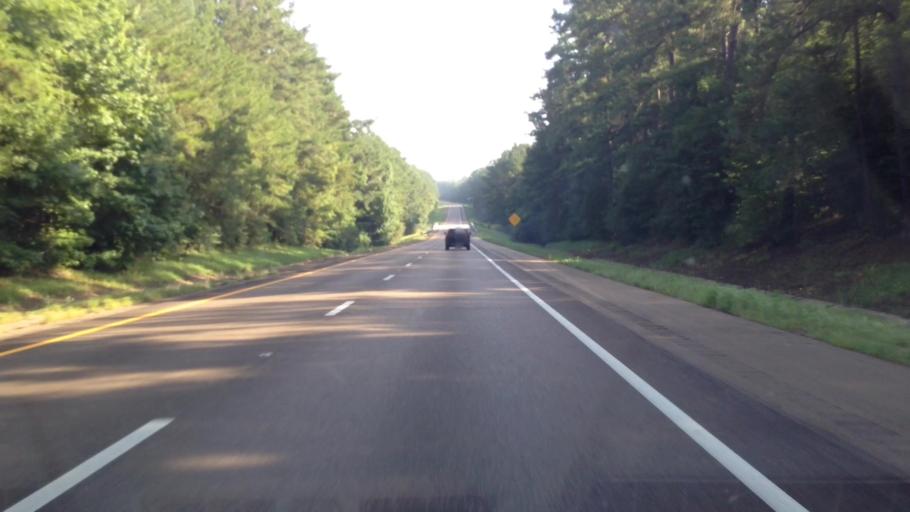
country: US
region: Mississippi
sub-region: Pike County
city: Summit
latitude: 31.3227
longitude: -90.4773
